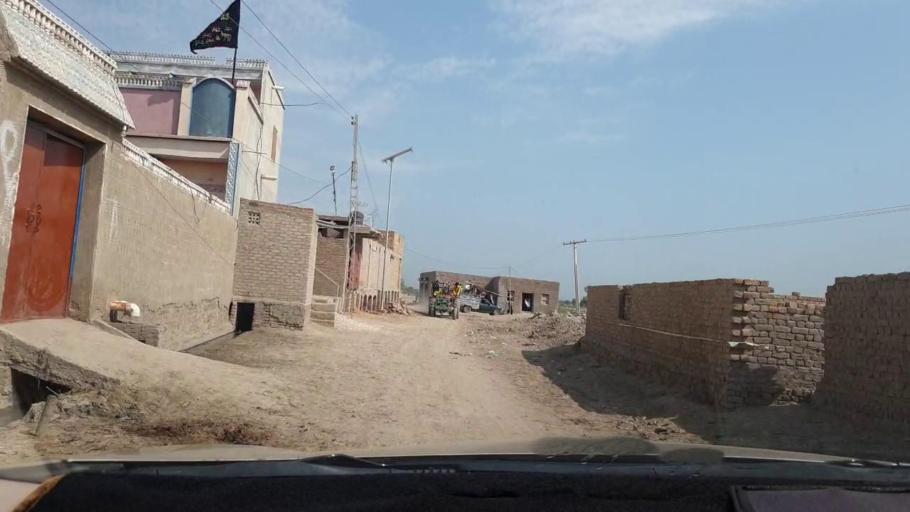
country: PK
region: Sindh
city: Larkana
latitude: 27.6679
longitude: 68.2227
